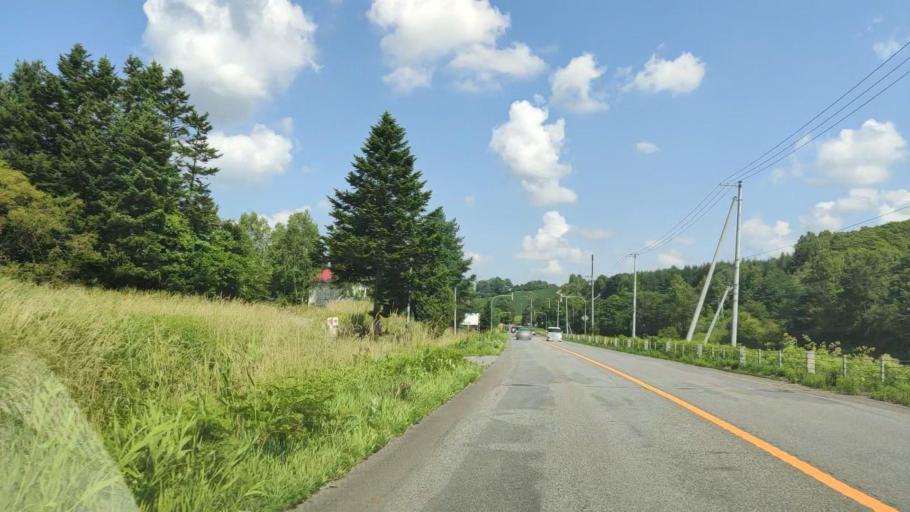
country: JP
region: Hokkaido
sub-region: Asahikawa-shi
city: Asahikawa
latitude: 43.5745
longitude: 142.4394
